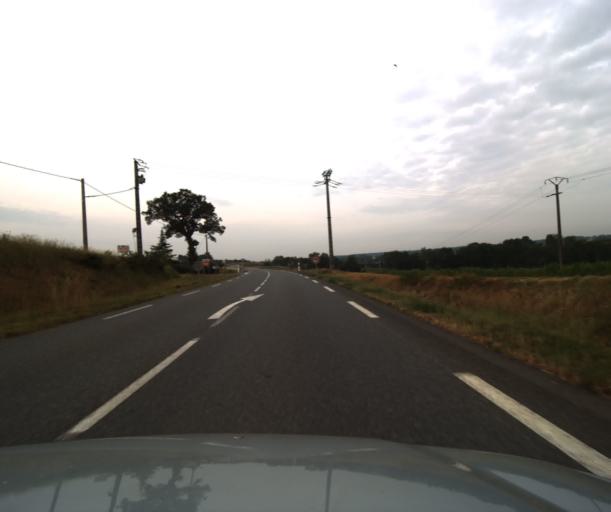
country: FR
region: Midi-Pyrenees
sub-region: Departement du Gers
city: Aubiet
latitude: 43.6590
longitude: 0.7867
